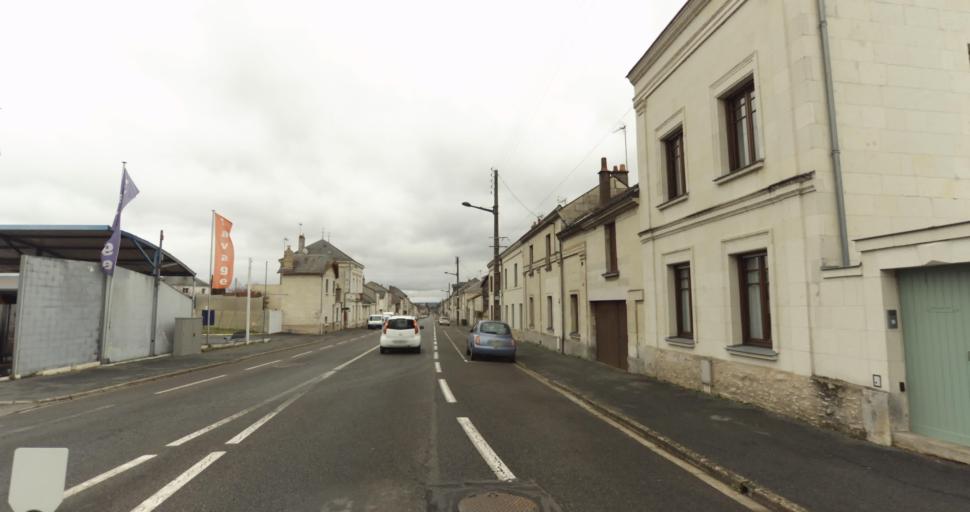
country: FR
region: Pays de la Loire
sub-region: Departement de Maine-et-Loire
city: Saumur
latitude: 47.2456
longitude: -0.0948
